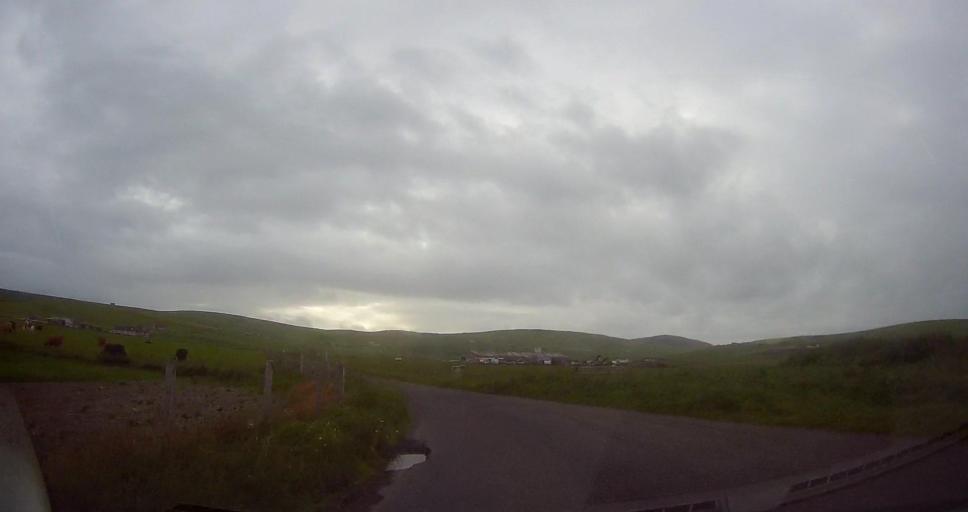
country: GB
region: Scotland
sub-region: Orkney Islands
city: Stromness
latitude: 58.9902
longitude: -3.2841
